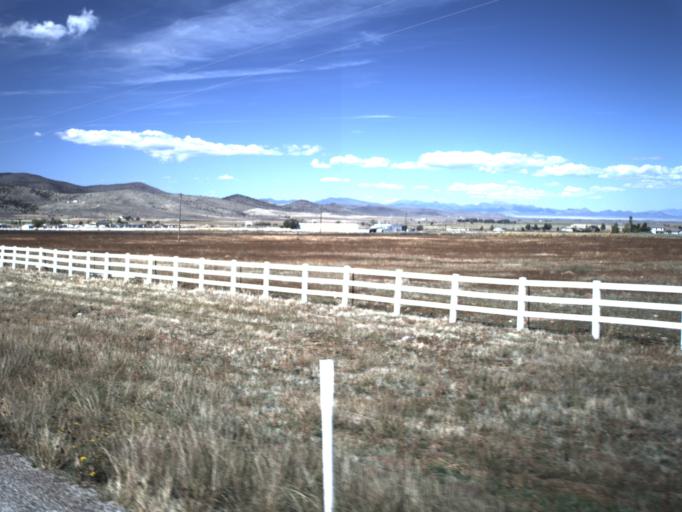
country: US
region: Utah
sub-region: Washington County
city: Enterprise
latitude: 37.5681
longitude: -113.6974
